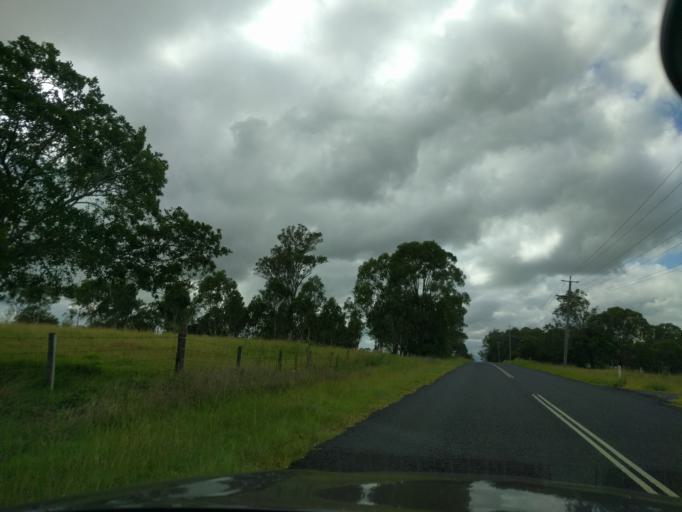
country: AU
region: Queensland
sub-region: Logan
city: Cedar Vale
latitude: -28.0014
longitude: 152.9887
